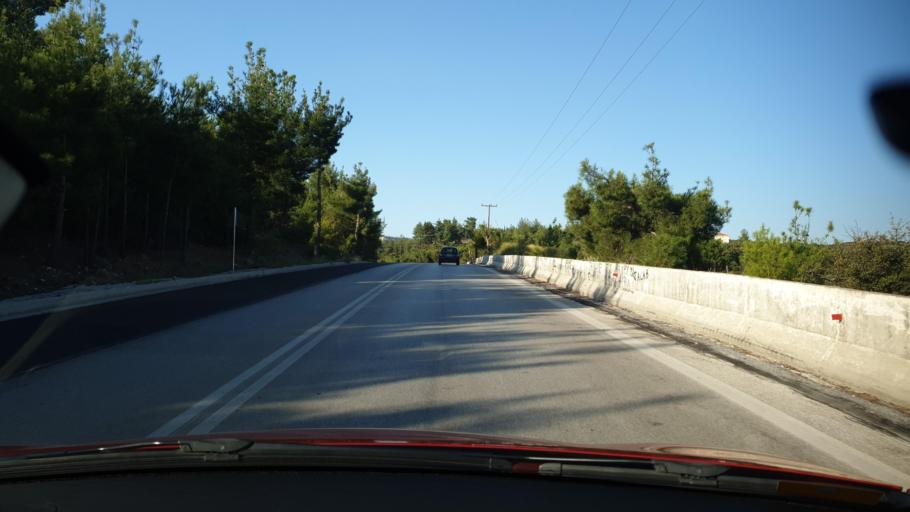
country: GR
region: Central Macedonia
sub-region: Nomos Thessalonikis
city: Panorama
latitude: 40.6039
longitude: 23.0504
